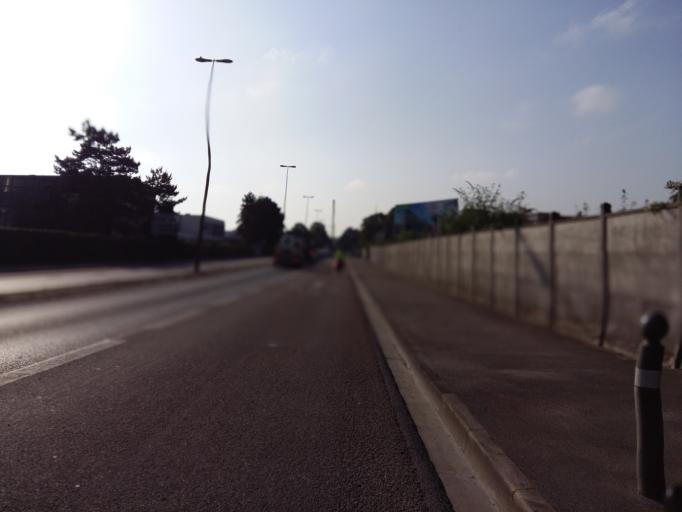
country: FR
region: Picardie
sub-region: Departement de la Somme
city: Amiens
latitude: 49.9013
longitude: 2.2849
